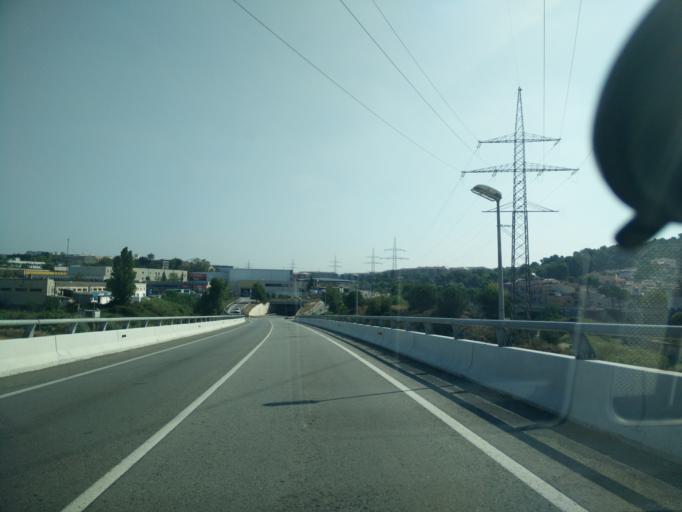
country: ES
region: Catalonia
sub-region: Provincia de Barcelona
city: Terrassa
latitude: 41.5324
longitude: 2.0322
